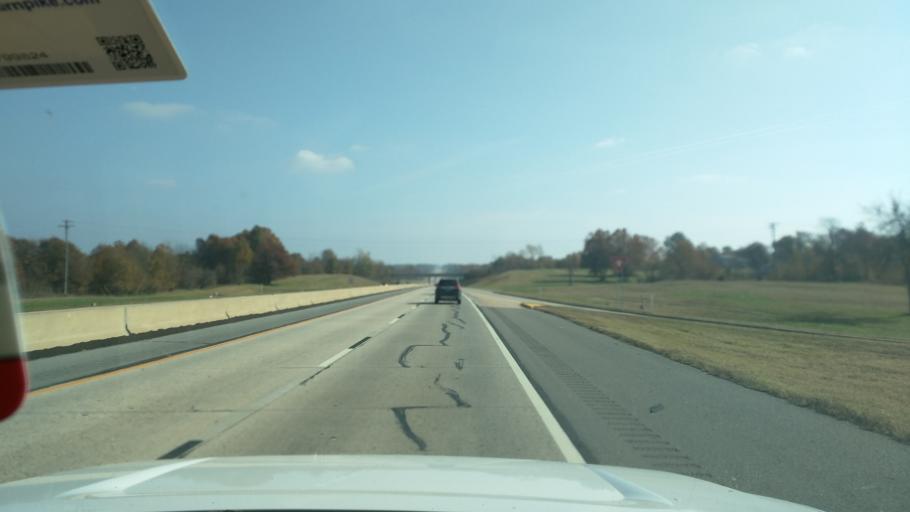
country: US
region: Oklahoma
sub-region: Muskogee County
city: Muskogee
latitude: 35.8426
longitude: -95.3989
